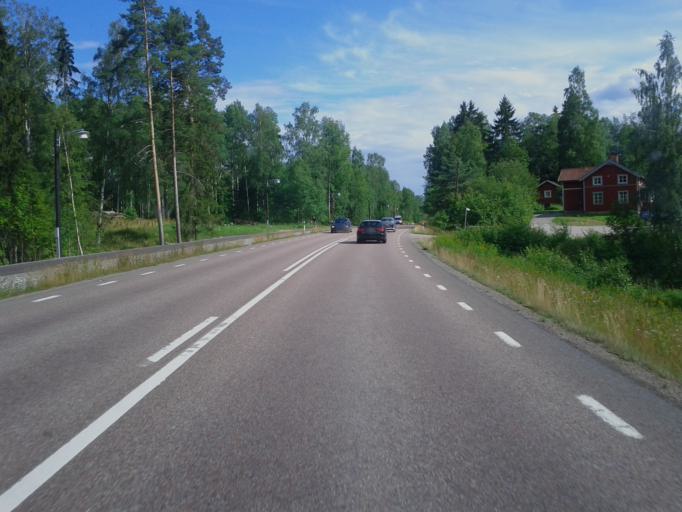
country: SE
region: Dalarna
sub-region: Faluns Kommun
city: Grycksbo
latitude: 60.6689
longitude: 15.5406
